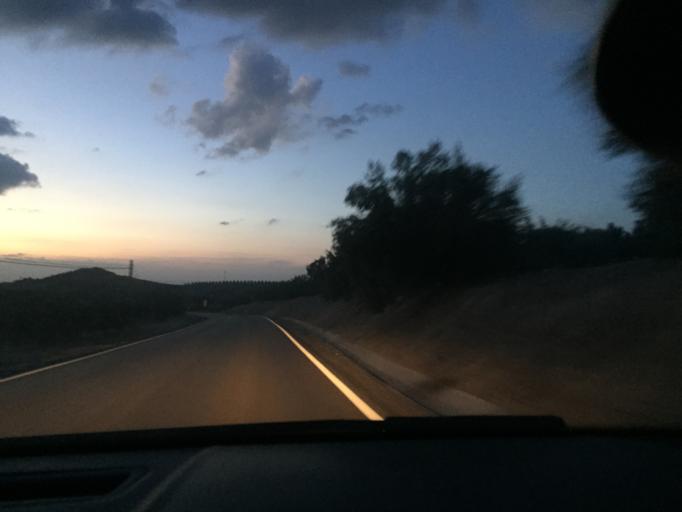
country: ES
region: Andalusia
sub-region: Provincia de Jaen
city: Mancha Real
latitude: 37.7967
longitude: -3.6481
